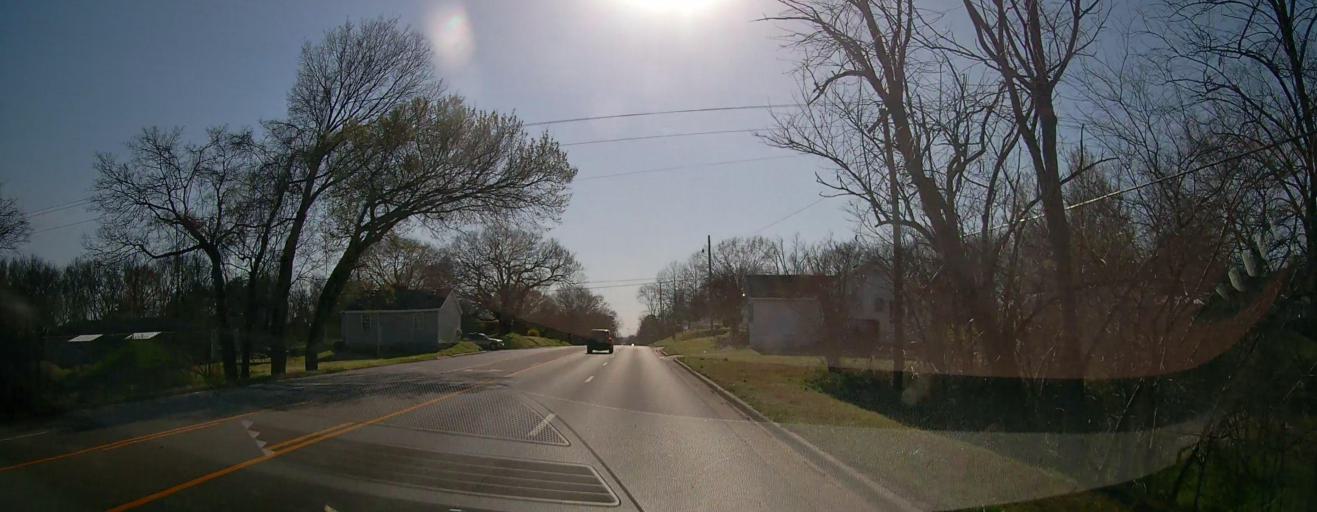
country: US
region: Alabama
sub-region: Lauderdale County
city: East Florence
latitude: 34.8079
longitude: -87.6406
